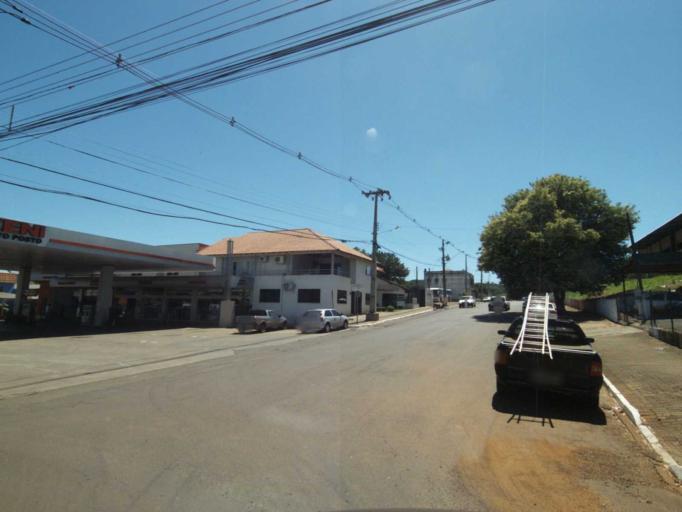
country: BR
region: Parana
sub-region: Coronel Vivida
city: Coronel Vivida
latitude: -25.9661
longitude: -52.8148
